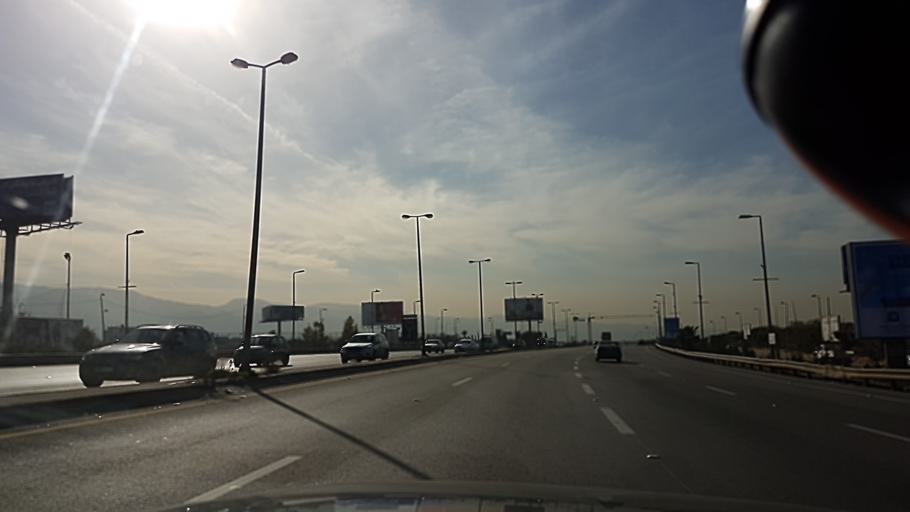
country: LB
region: Mont-Liban
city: Baabda
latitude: 33.8388
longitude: 35.4945
